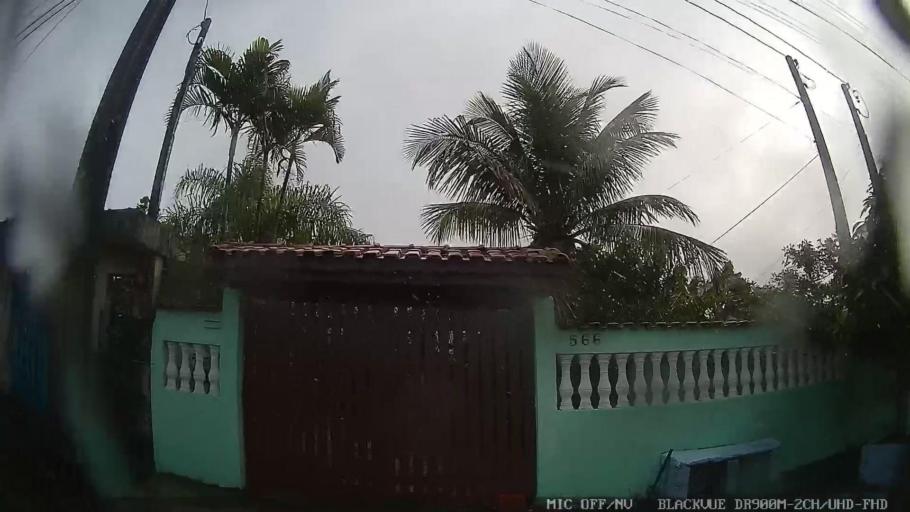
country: BR
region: Sao Paulo
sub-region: Peruibe
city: Peruibe
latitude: -24.2377
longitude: -46.9028
